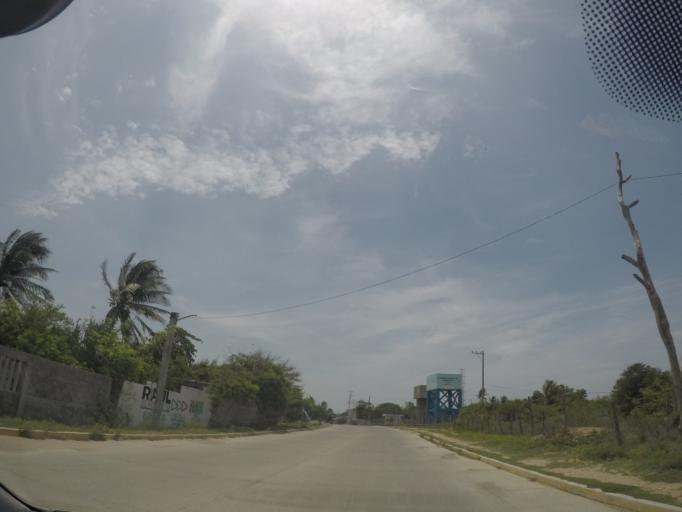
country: MX
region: Oaxaca
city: San Mateo del Mar
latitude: 16.2105
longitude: -94.9886
